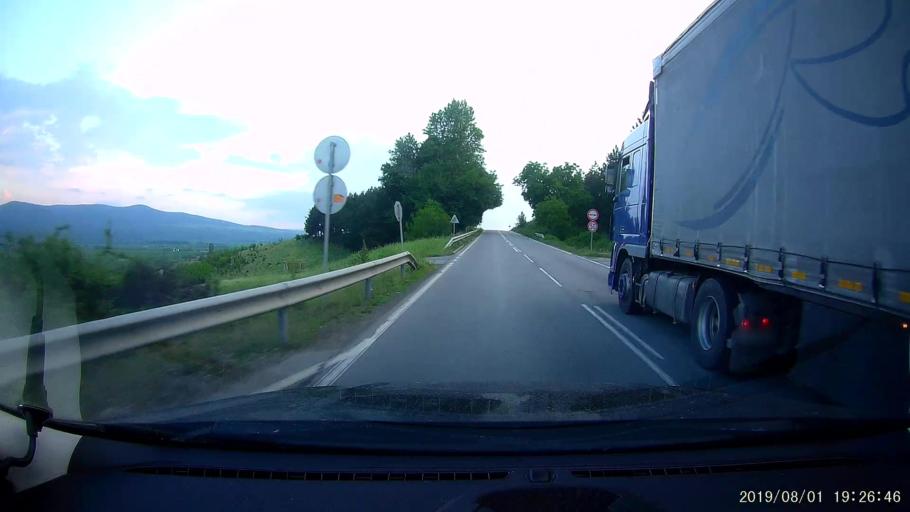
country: BG
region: Burgas
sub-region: Obshtina Sungurlare
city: Sungurlare
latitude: 42.8546
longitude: 26.9379
